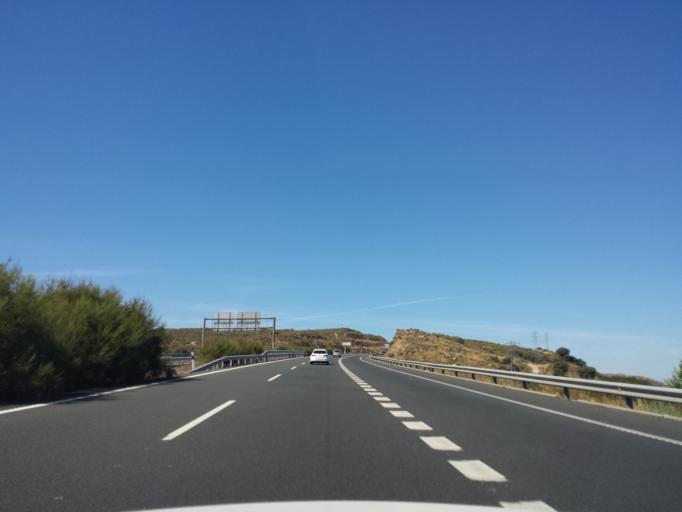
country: ES
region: Extremadura
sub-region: Provincia de Caceres
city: Navalmoral de la Mata
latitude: 39.8888
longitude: -5.5177
